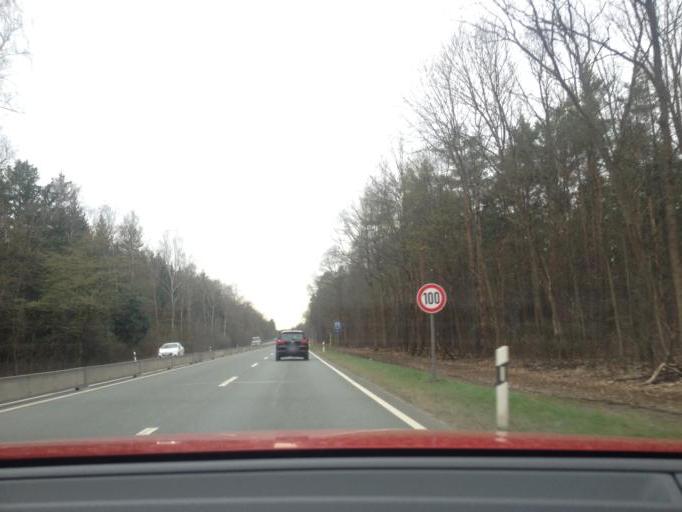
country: DE
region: Bavaria
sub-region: Regierungsbezirk Mittelfranken
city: Feucht
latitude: 49.4116
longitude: 11.1803
